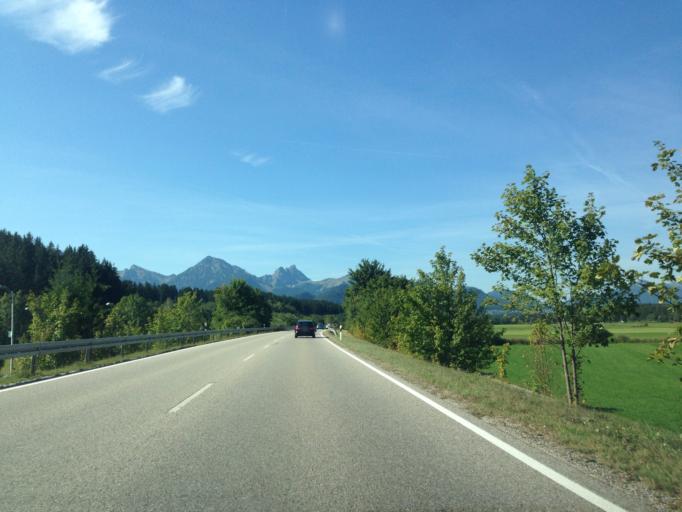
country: DE
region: Bavaria
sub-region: Swabia
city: Fuessen
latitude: 47.5825
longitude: 10.6984
